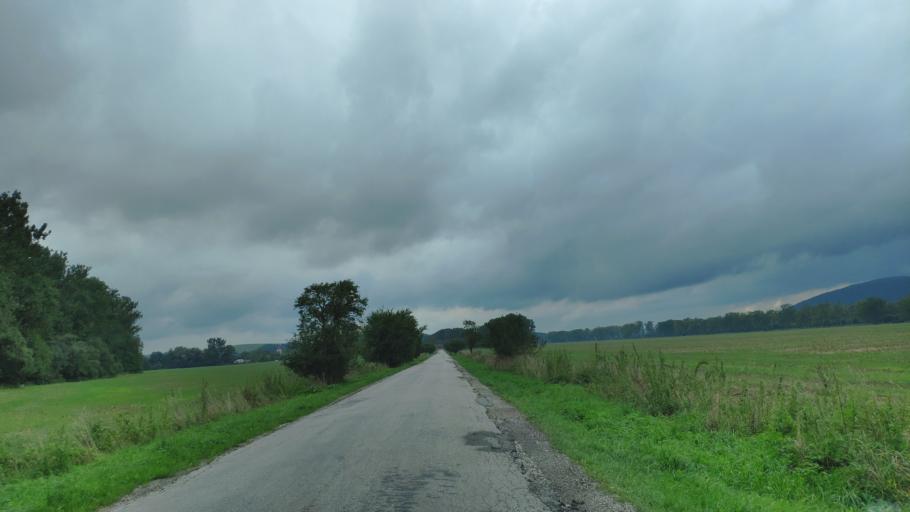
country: SK
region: Kosicky
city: Moldava nad Bodvou
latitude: 48.5865
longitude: 20.8949
